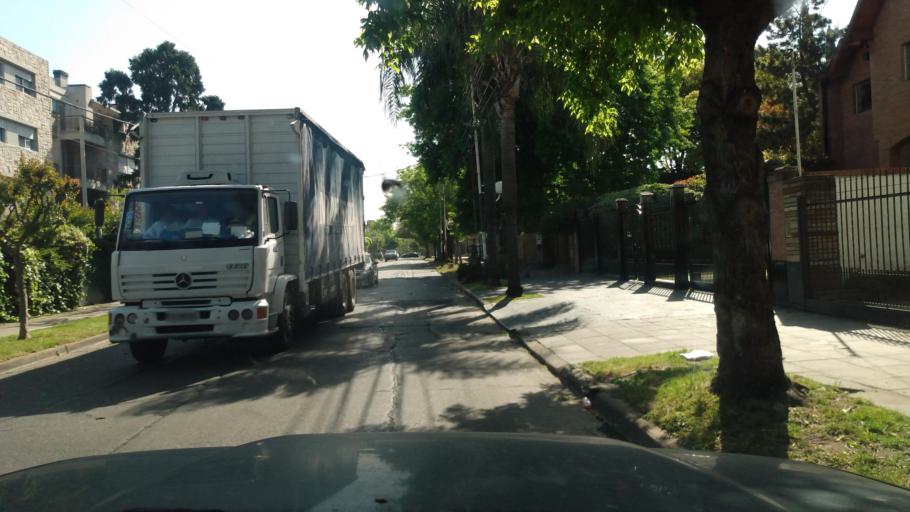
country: AR
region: Buenos Aires
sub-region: Partido de Moron
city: Moron
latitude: -34.6494
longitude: -58.5926
